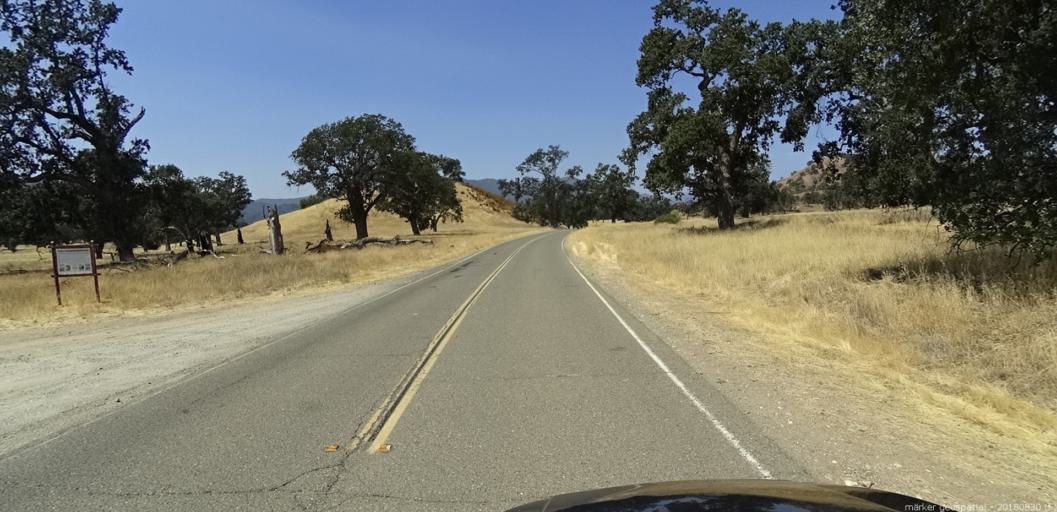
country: US
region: California
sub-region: Monterey County
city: King City
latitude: 35.9613
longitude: -121.2884
